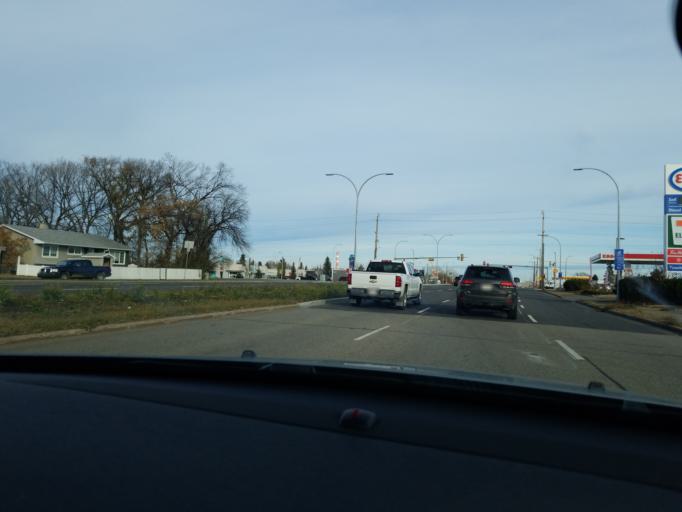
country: CA
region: Alberta
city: Edmonton
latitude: 53.5411
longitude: -113.4216
